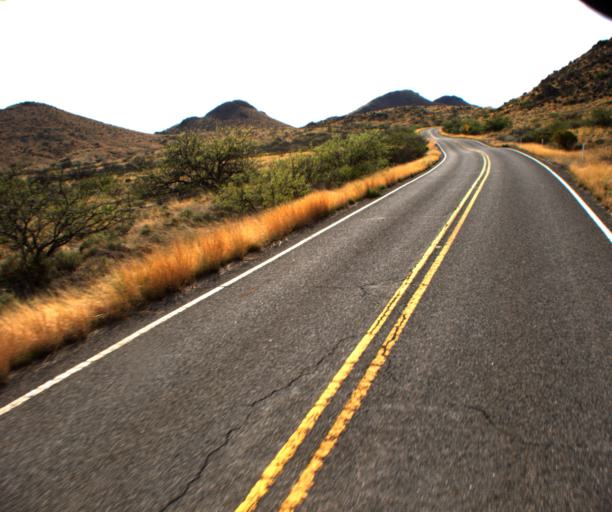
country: US
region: Arizona
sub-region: Cochise County
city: Willcox
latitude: 32.1673
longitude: -109.5843
